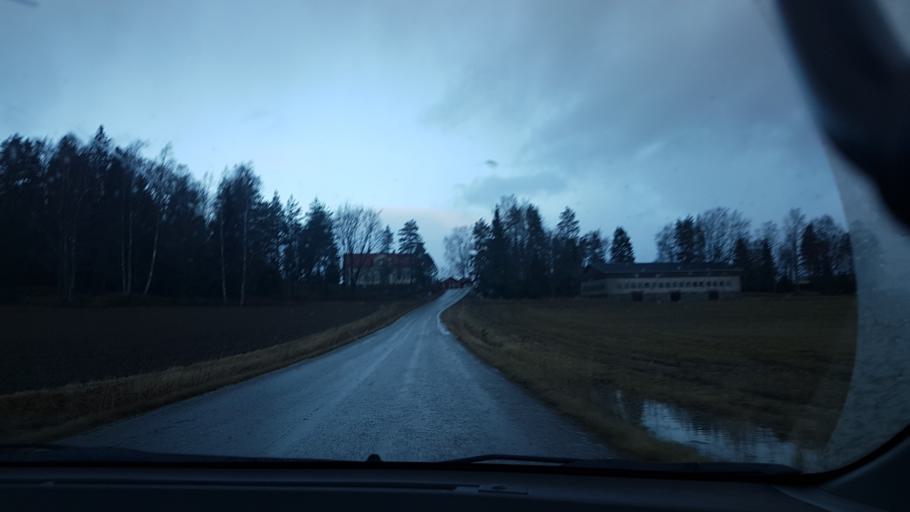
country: FI
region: Uusimaa
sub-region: Helsinki
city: Lohja
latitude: 60.2107
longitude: 24.1009
